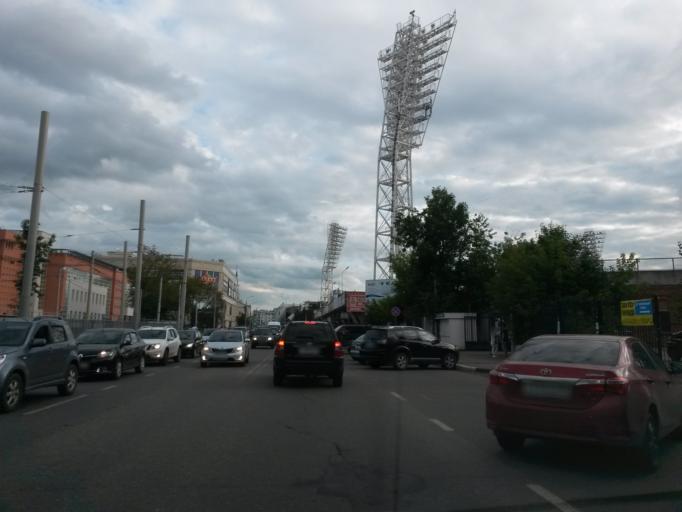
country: RU
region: Jaroslavl
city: Yaroslavl
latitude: 57.6300
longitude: 39.8694
